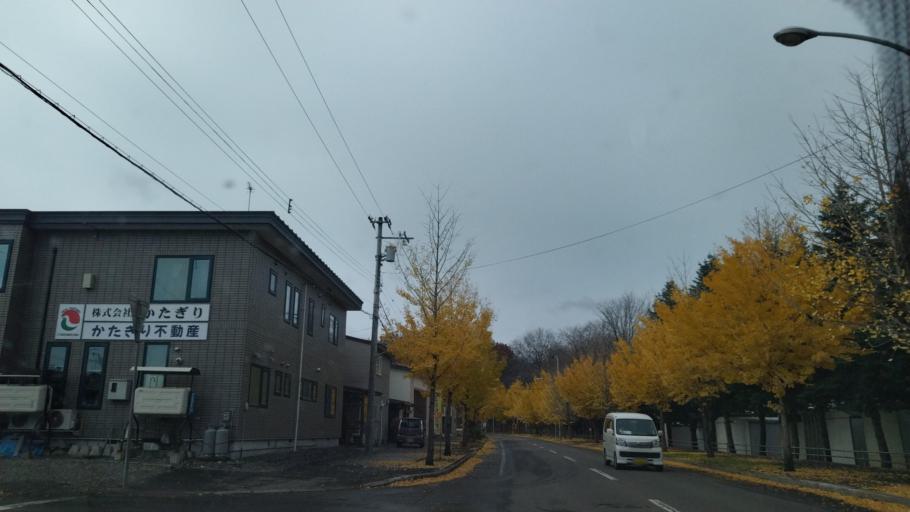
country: JP
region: Hokkaido
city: Obihiro
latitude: 42.8858
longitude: 143.1887
